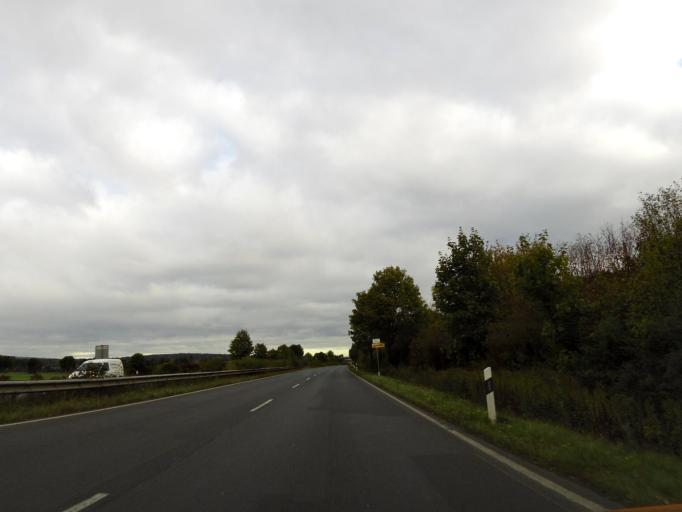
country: DE
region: Lower Saxony
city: Goettingen
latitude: 51.5609
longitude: 9.9202
